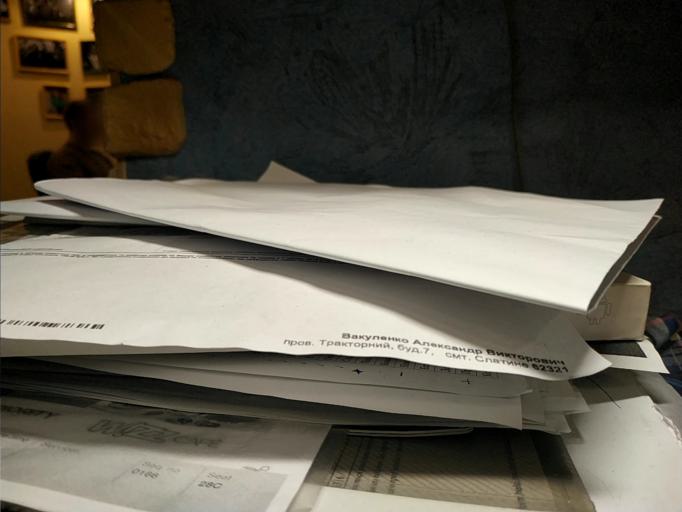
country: RU
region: Tverskaya
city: Zubtsov
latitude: 56.1075
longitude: 34.6459
